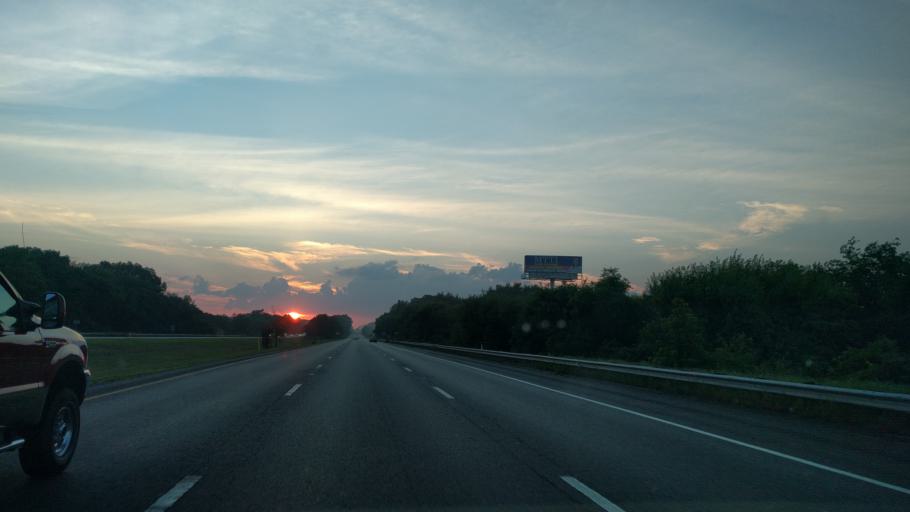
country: US
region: Rhode Island
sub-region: Bristol County
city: Barrington
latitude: 41.7836
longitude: -71.2911
